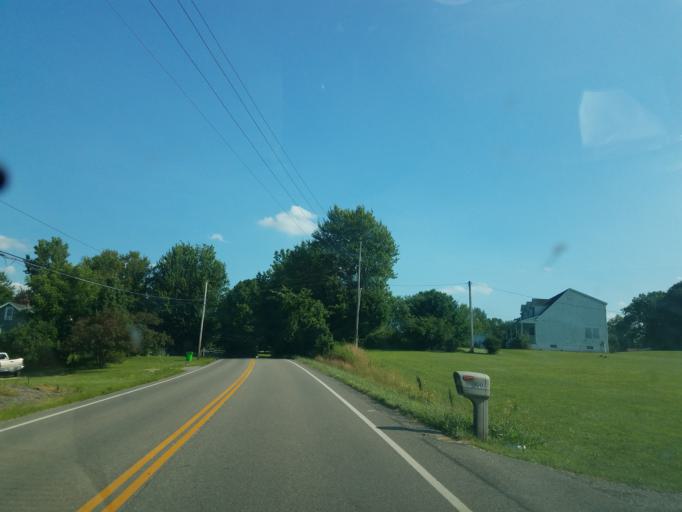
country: US
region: Ohio
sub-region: Summit County
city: Greensburg
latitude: 40.9472
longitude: -81.4363
